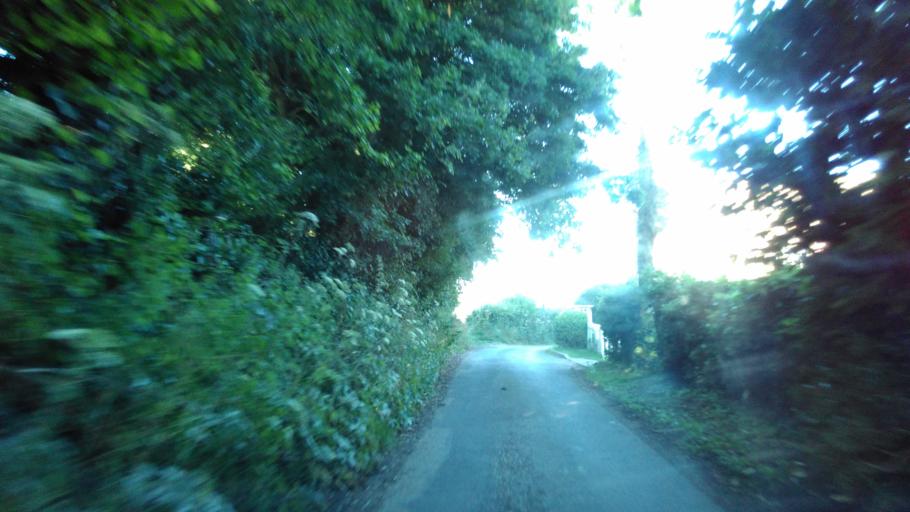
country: GB
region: England
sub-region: Kent
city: Chartham
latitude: 51.2461
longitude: 0.9932
